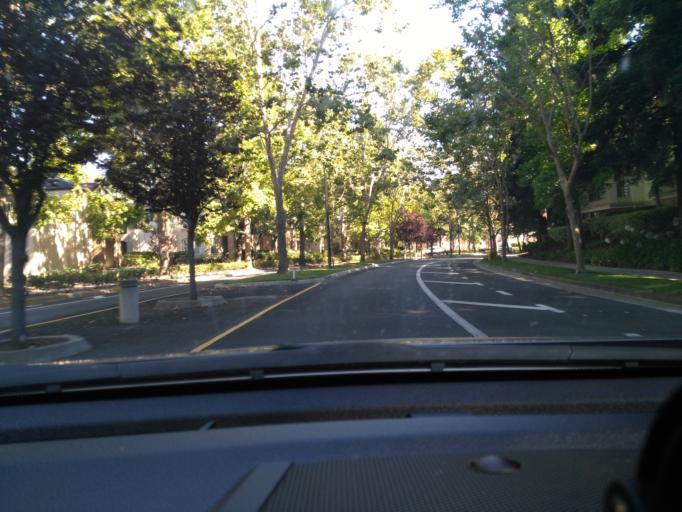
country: US
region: California
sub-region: Santa Clara County
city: Milpitas
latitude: 37.4012
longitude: -121.9217
